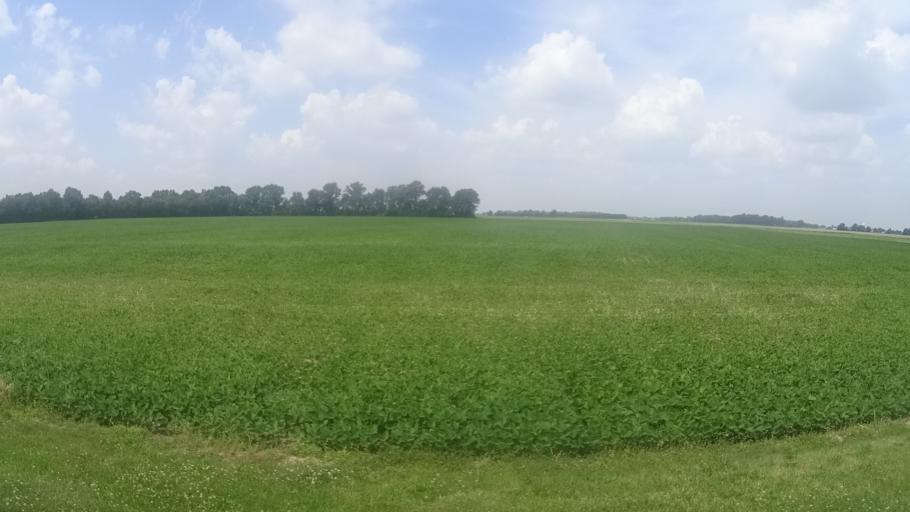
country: US
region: Ohio
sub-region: Huron County
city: Monroeville
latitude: 41.3173
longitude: -82.7160
